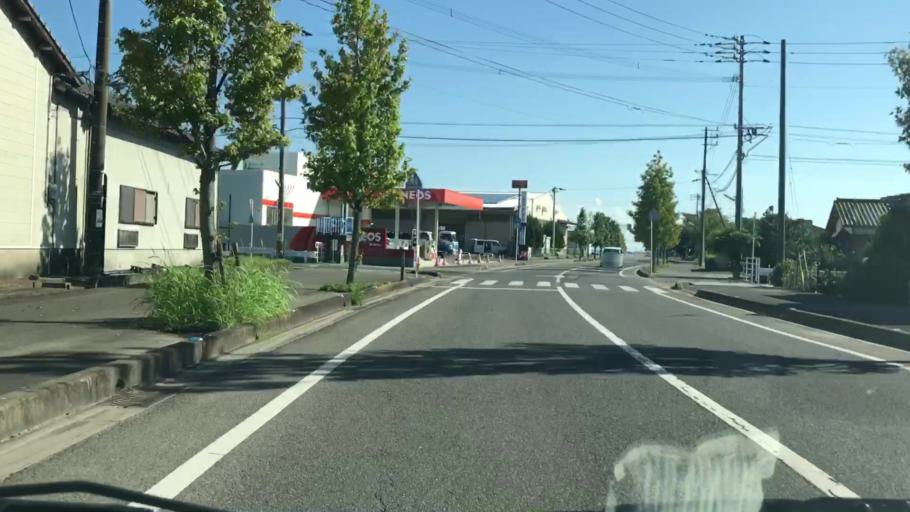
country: JP
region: Saga Prefecture
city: Okawa
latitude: 33.1821
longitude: 130.3136
